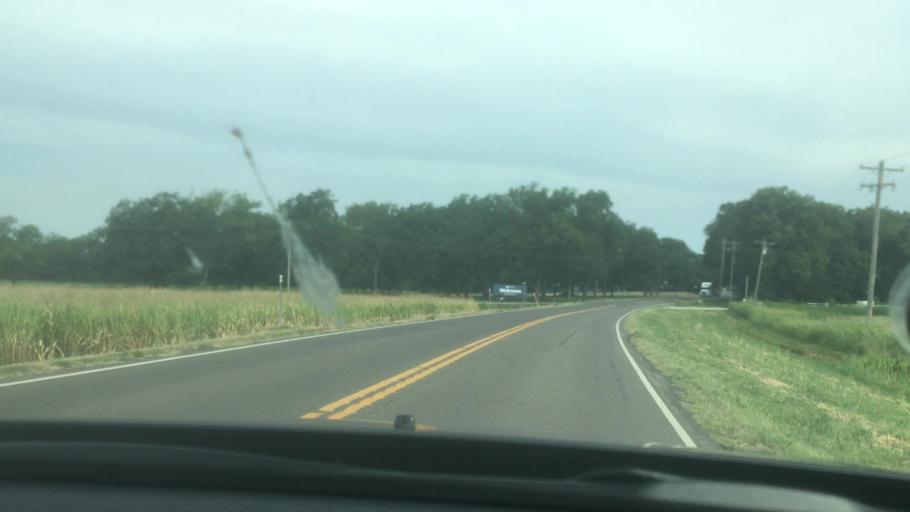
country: US
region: Oklahoma
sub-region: Garvin County
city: Pauls Valley
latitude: 34.7408
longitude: -97.2772
